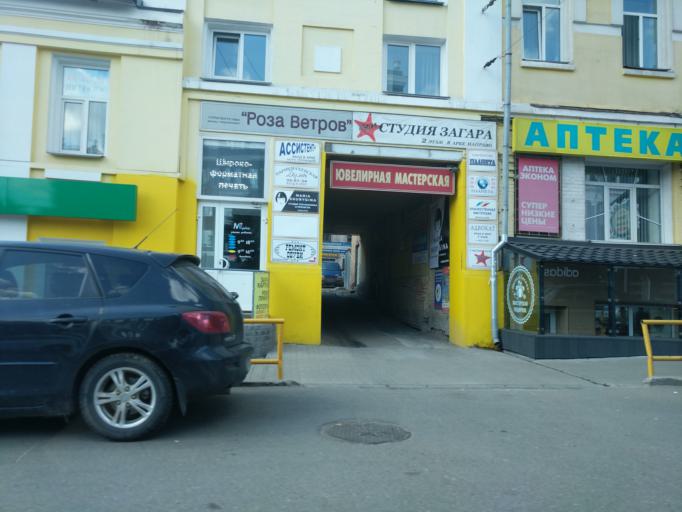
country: RU
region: Kirov
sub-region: Kirovo-Chepetskiy Rayon
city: Kirov
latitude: 58.6042
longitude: 49.6808
